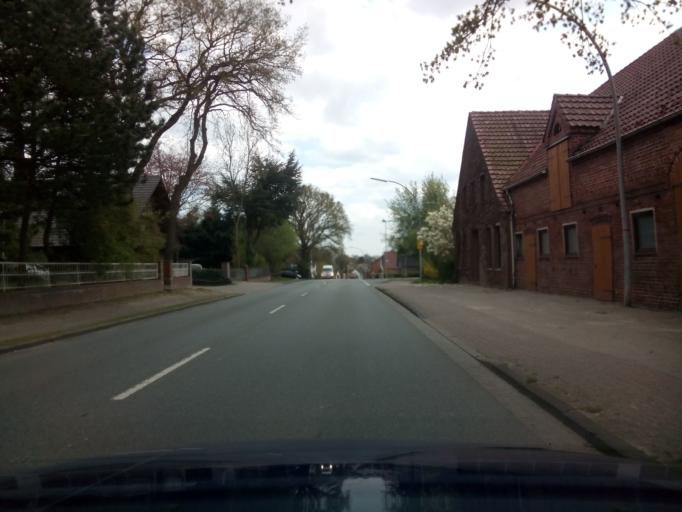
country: DE
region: Lower Saxony
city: Osterholz-Scharmbeck
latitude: 53.2380
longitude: 8.7836
